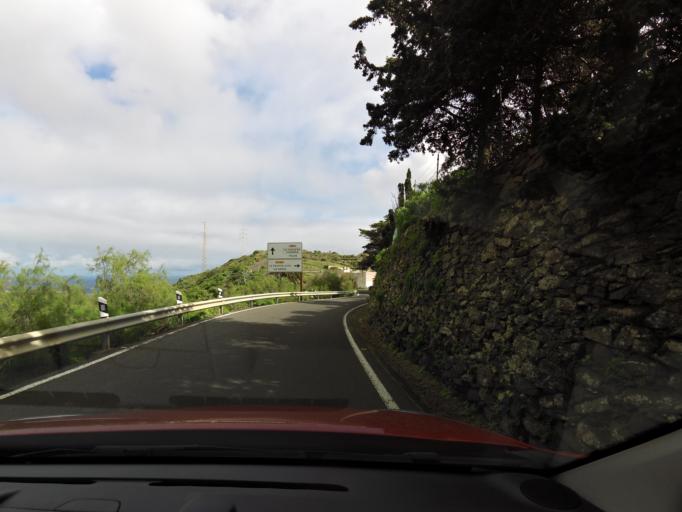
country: ES
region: Canary Islands
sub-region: Provincia de Las Palmas
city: Telde
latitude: 28.0199
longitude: -15.4562
